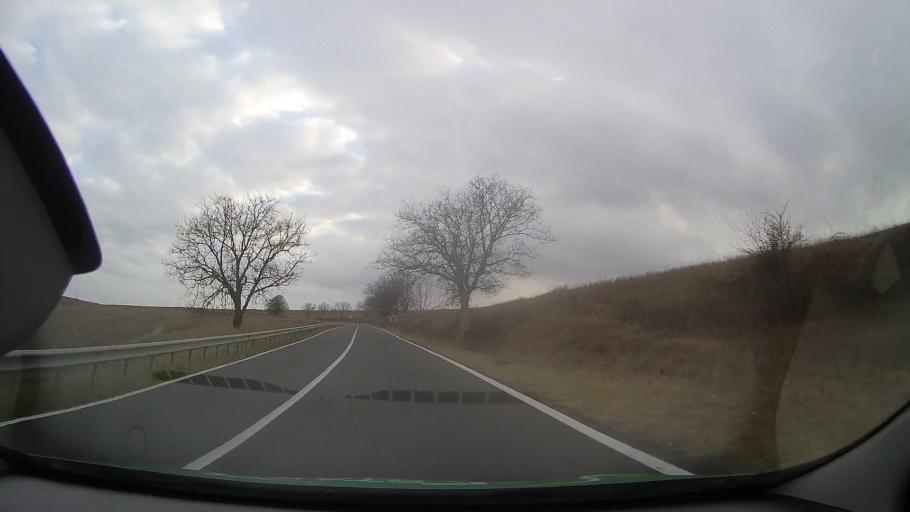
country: RO
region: Constanta
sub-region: Comuna Deleni
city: Deleni
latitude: 44.0971
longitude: 28.0170
